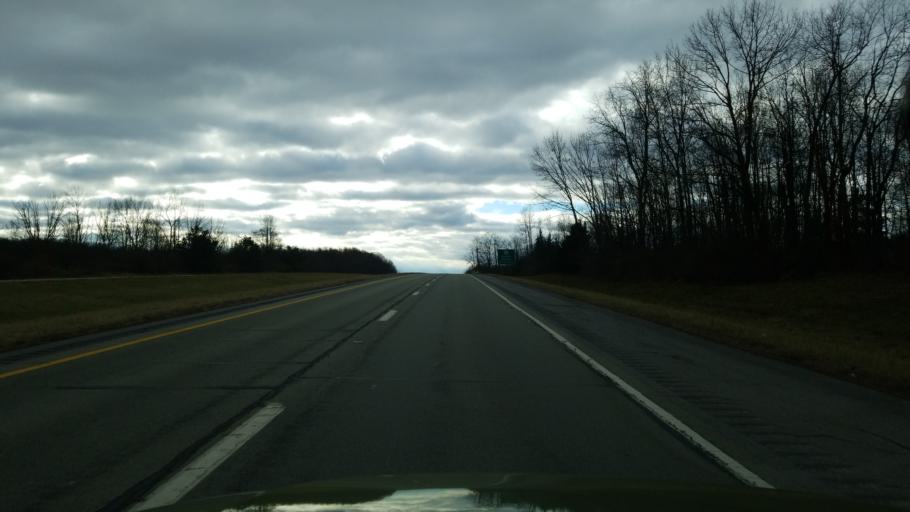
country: US
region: Pennsylvania
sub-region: Indiana County
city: Chevy Chase Heights
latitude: 40.6485
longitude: -79.1168
